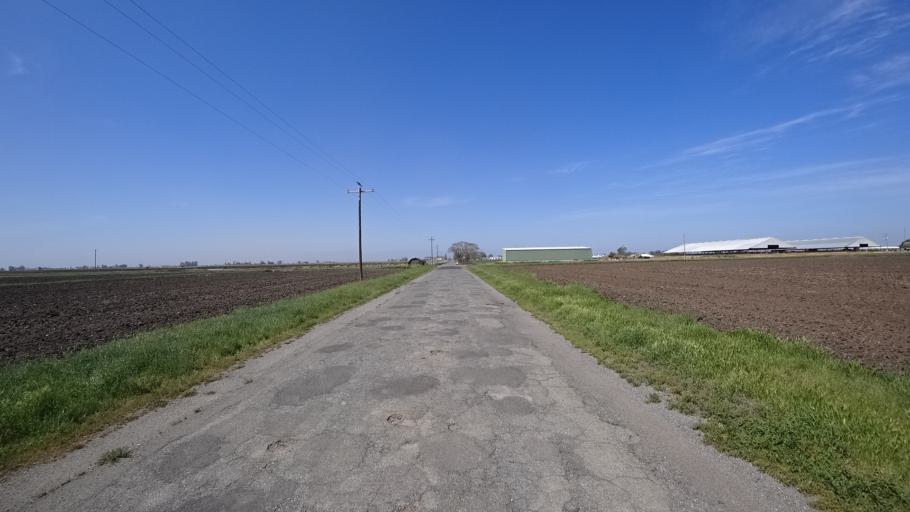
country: US
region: California
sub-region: Glenn County
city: Willows
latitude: 39.5727
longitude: -122.0824
